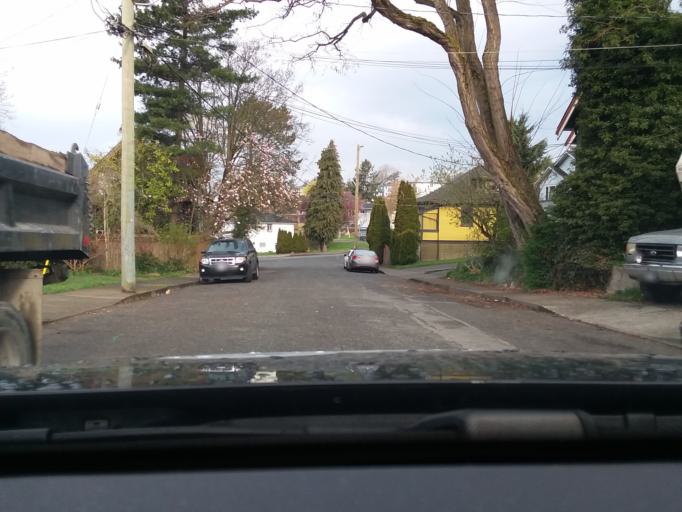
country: CA
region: British Columbia
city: Victoria
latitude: 48.4385
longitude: -123.3925
